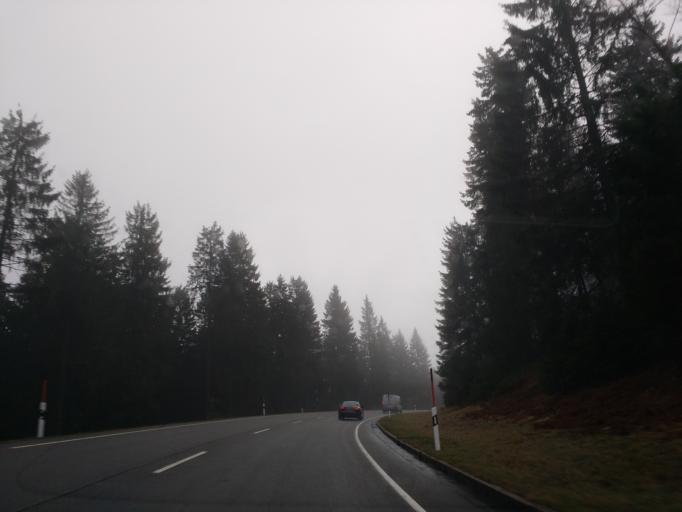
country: DE
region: Baden-Wuerttemberg
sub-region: Freiburg Region
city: Bad Peterstal-Griesbach
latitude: 48.4975
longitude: 8.2417
